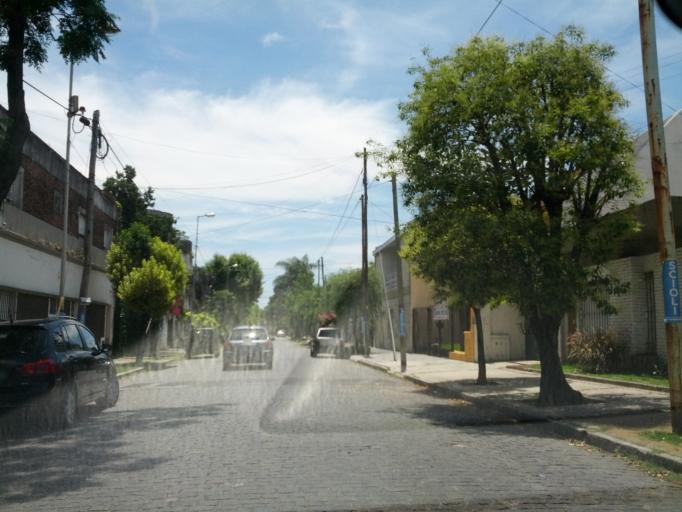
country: AR
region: Buenos Aires
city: Caseros
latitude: -34.6352
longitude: -58.5740
